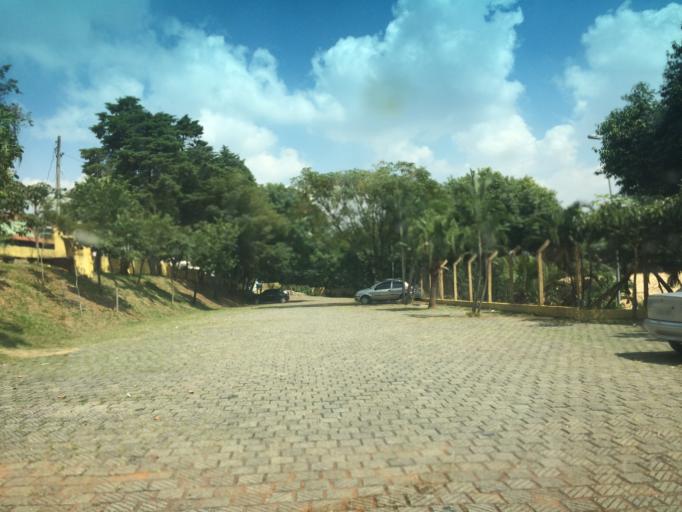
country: BR
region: Sao Paulo
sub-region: Guarulhos
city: Guarulhos
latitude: -23.4430
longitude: -46.5525
